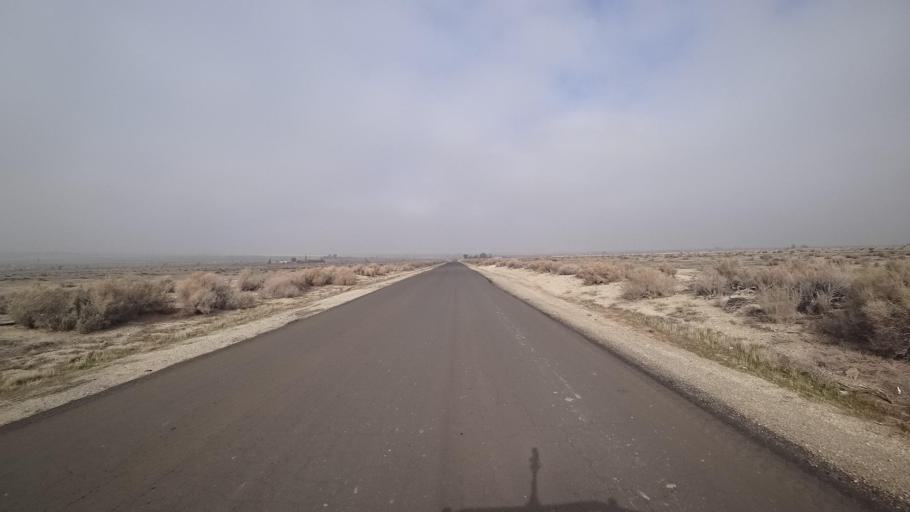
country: US
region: California
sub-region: Kern County
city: Maricopa
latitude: 35.0406
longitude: -119.3670
